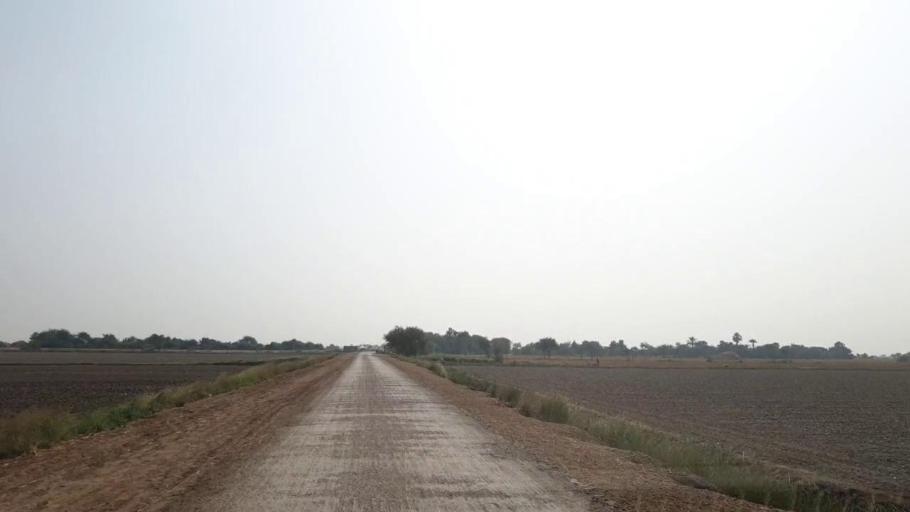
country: PK
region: Sindh
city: Matli
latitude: 24.9774
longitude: 68.5836
